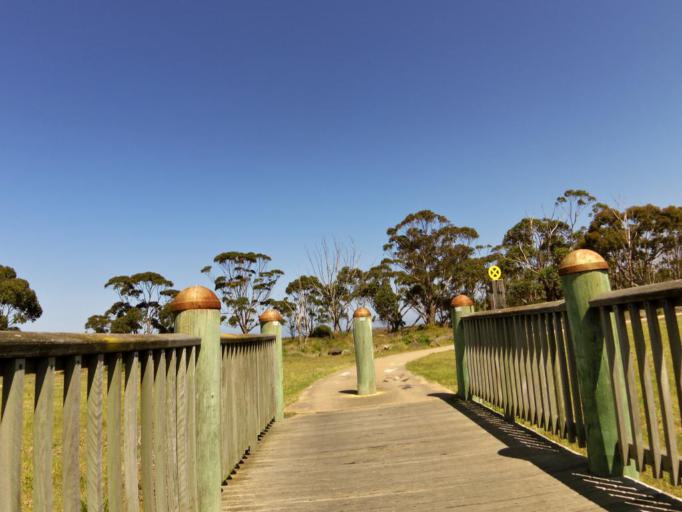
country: AU
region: Victoria
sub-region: Hobsons Bay
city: Altona Meadows
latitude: -37.8799
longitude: 144.8033
